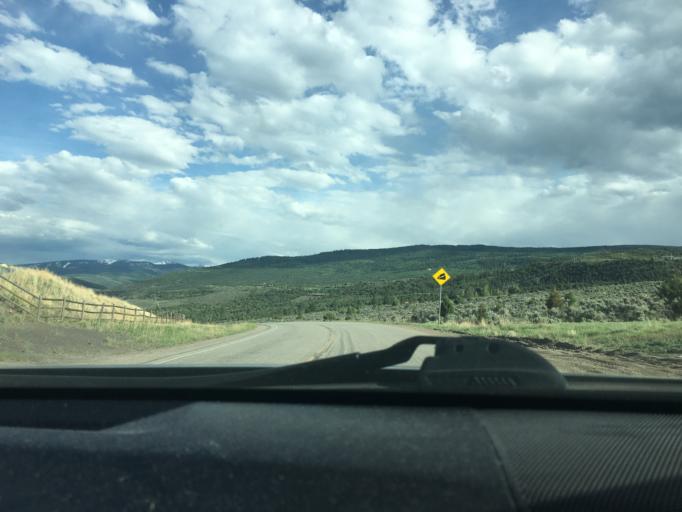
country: US
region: Colorado
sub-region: Eagle County
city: Edwards
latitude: 39.7072
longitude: -106.6858
